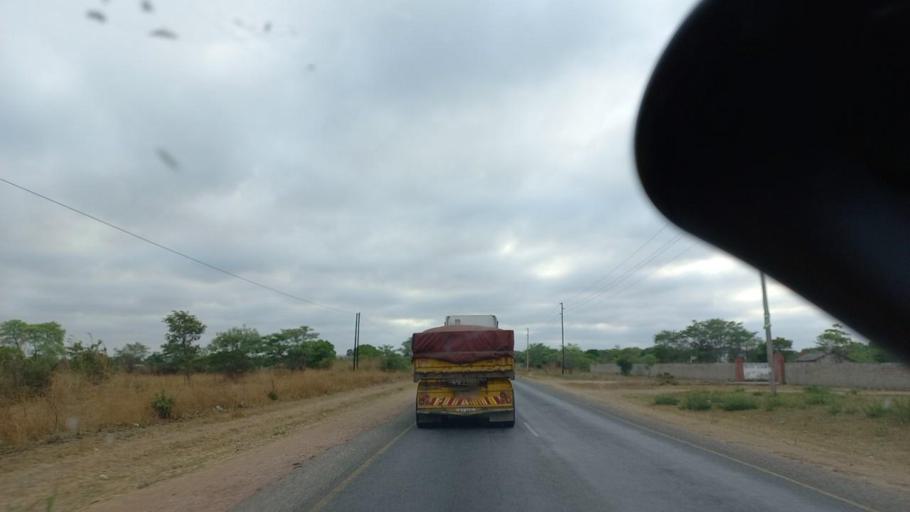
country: ZM
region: Lusaka
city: Chongwe
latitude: -15.3522
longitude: 28.5533
